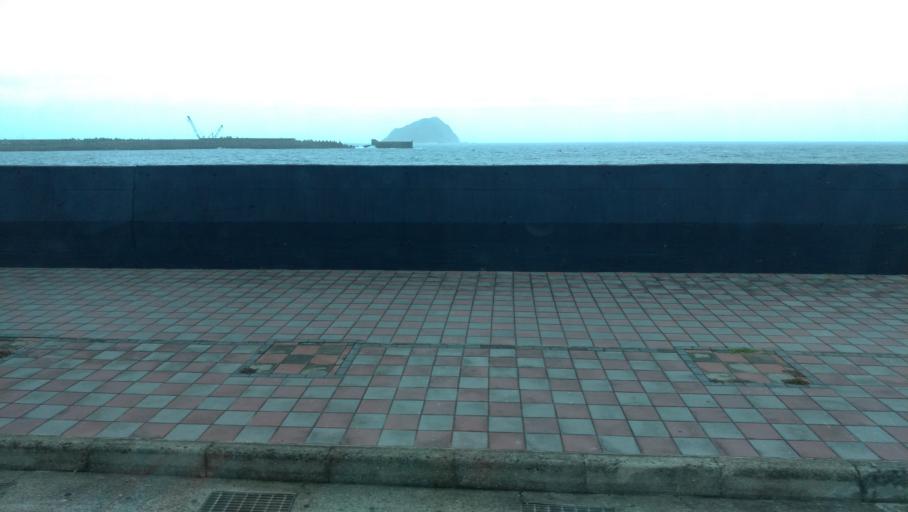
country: TW
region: Taiwan
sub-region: Keelung
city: Keelung
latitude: 25.1511
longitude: 121.7784
